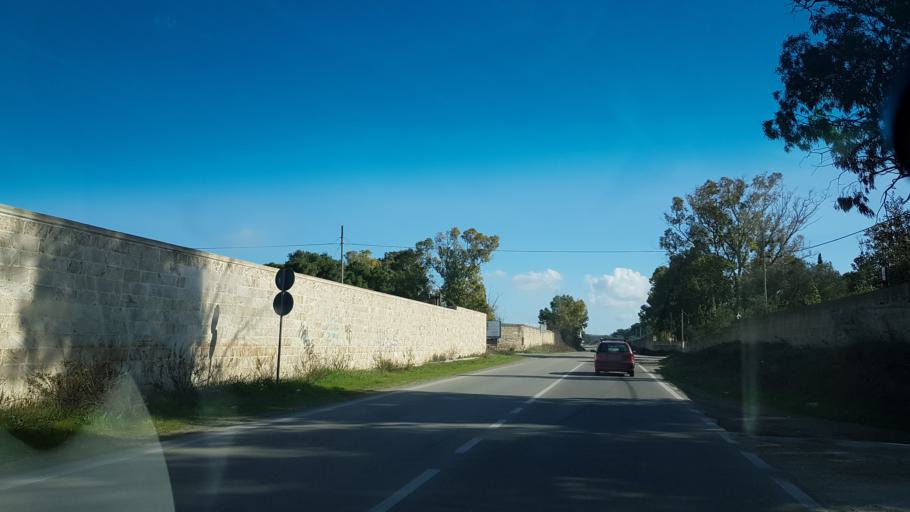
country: IT
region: Apulia
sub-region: Provincia di Lecce
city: Arnesano
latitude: 40.3579
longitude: 18.1202
